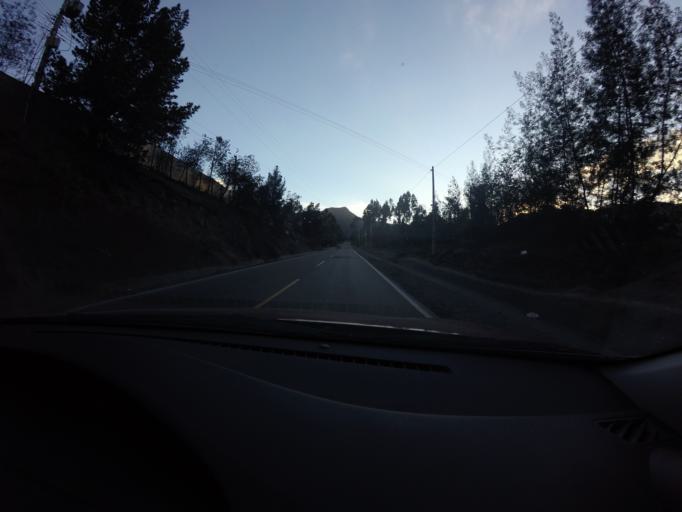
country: CO
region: Cundinamarca
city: Sutatausa
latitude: 5.2213
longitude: -73.8608
